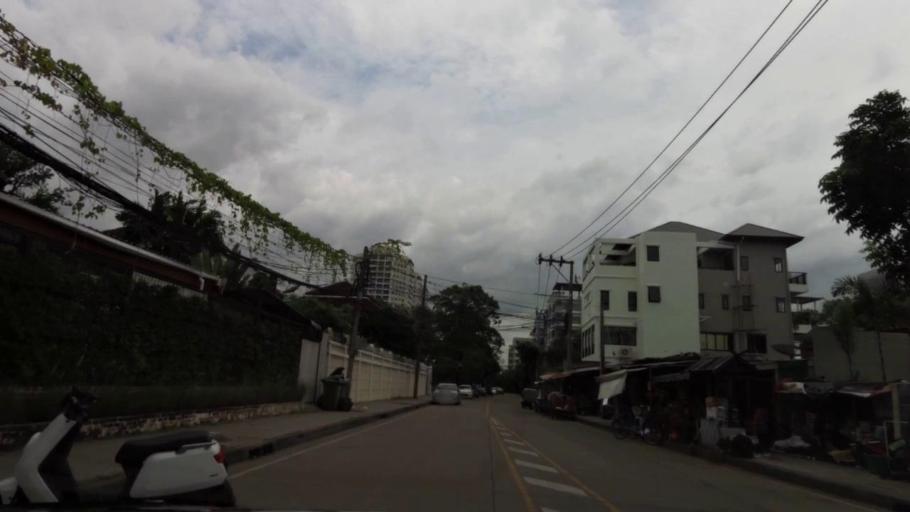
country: TH
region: Bangkok
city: Bang Kapi
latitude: 13.7537
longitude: 100.6397
